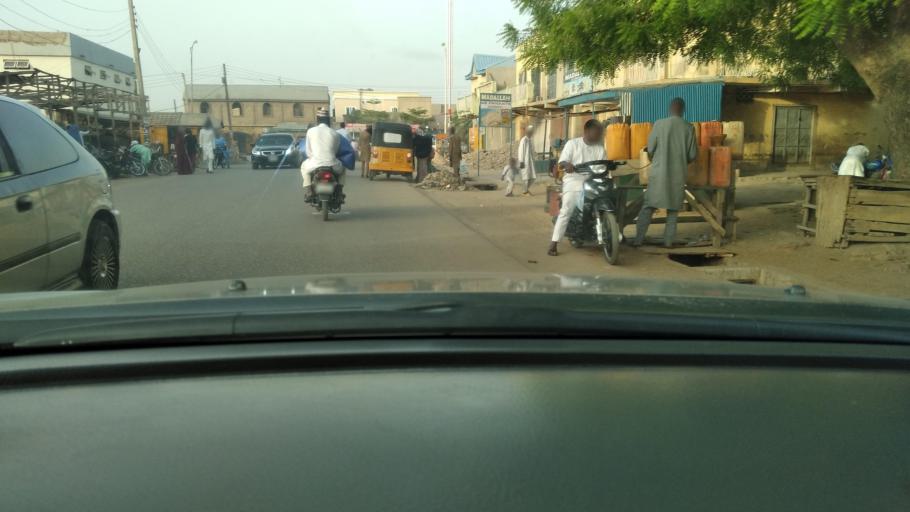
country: NG
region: Kano
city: Kano
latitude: 11.9619
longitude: 8.5262
